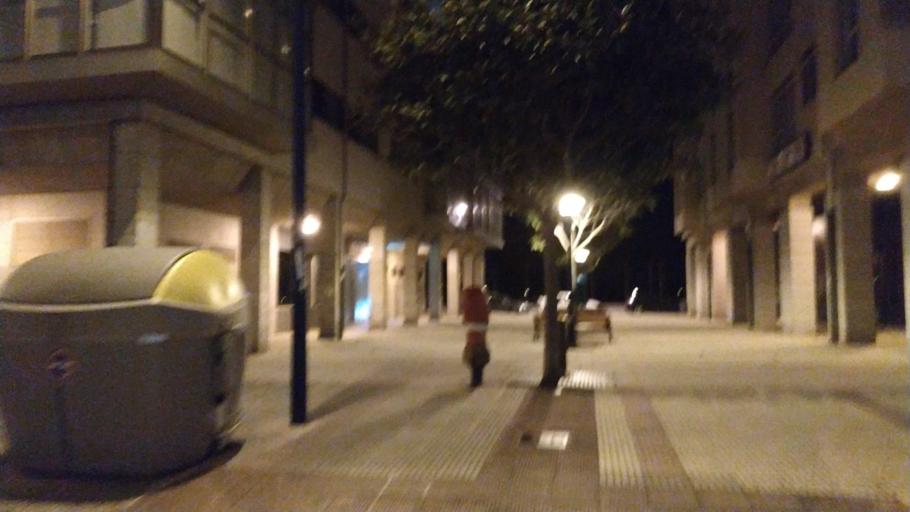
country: ES
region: Galicia
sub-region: Provincia da Coruna
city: Cambre
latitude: 43.3181
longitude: -8.3672
